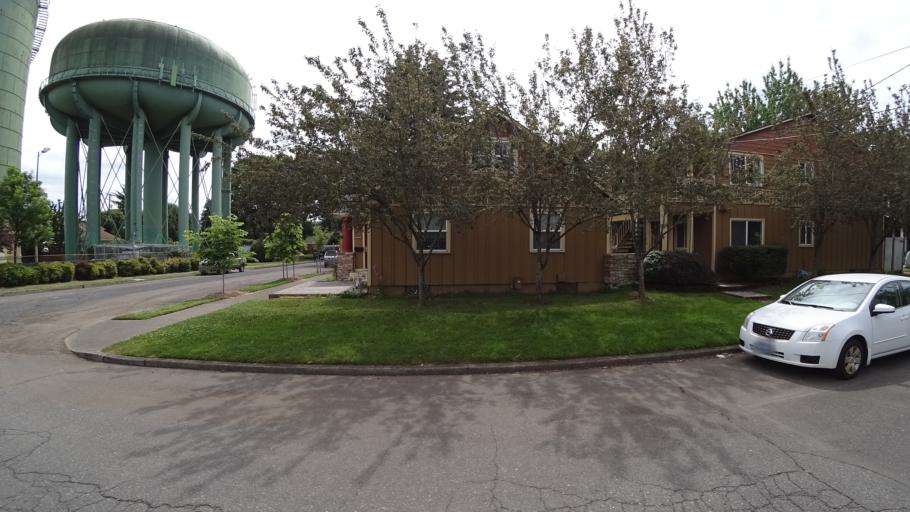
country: US
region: Oregon
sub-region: Washington County
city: West Haven
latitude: 45.5868
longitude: -122.7516
